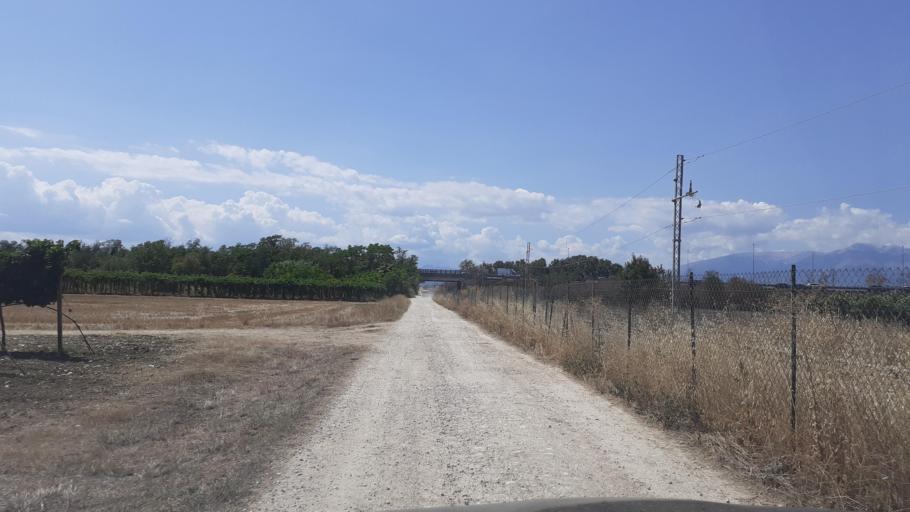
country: IT
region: Abruzzo
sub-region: Provincia di Chieti
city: Fossacesia
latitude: 42.2105
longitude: 14.4967
